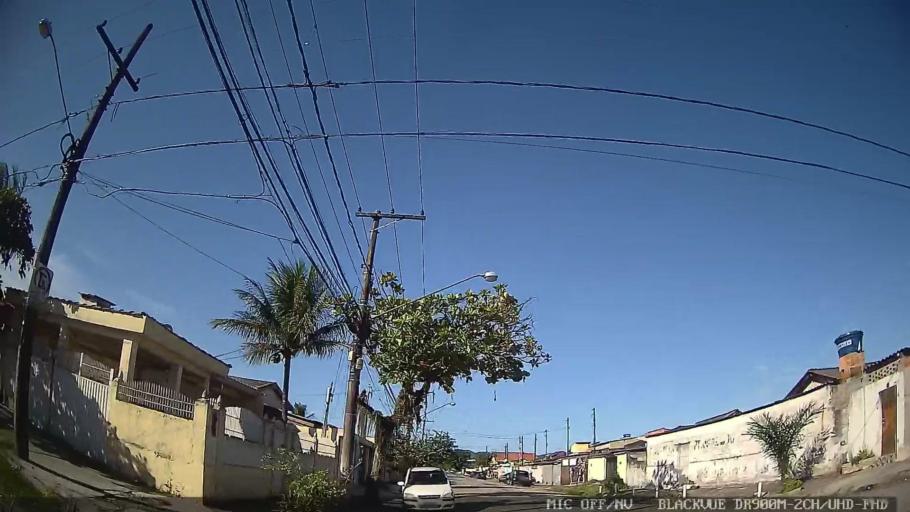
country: BR
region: Sao Paulo
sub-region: Guaruja
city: Guaruja
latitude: -23.9590
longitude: -46.2862
